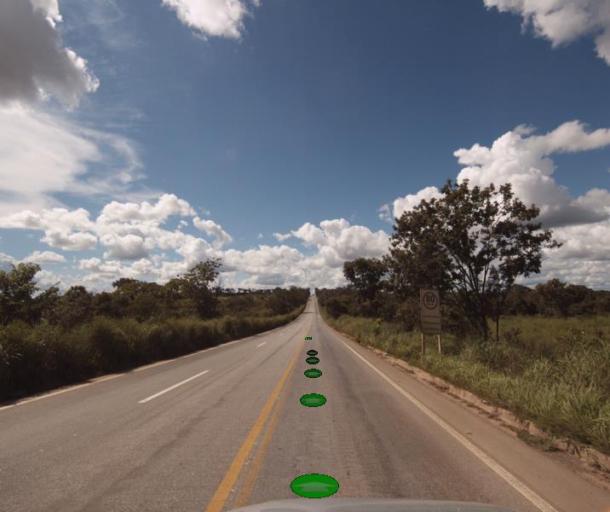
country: BR
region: Goias
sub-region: Porangatu
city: Porangatu
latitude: -13.4748
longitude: -49.1361
